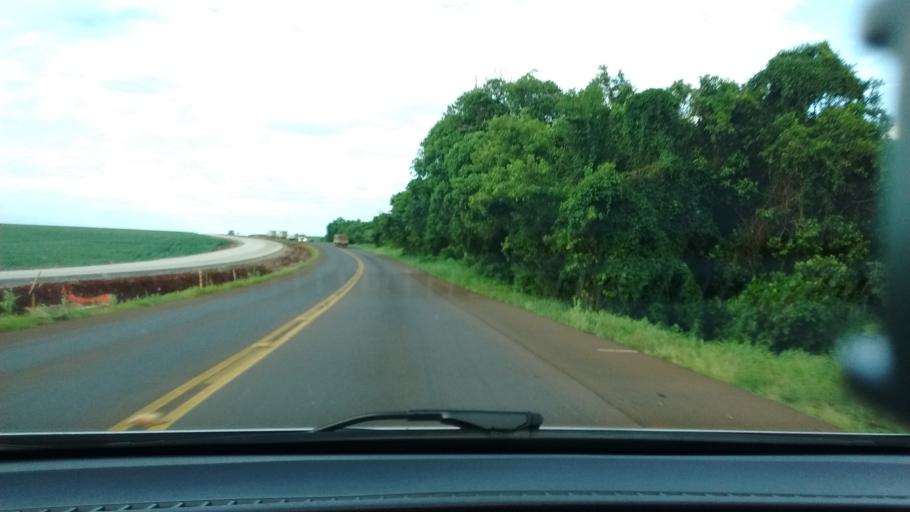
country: BR
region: Parana
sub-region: Cascavel
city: Cascavel
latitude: -25.0643
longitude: -53.5671
